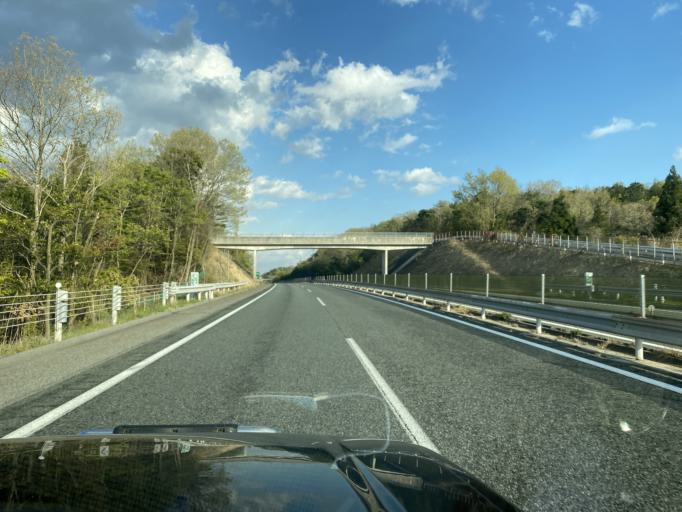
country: JP
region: Hyogo
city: Sandacho
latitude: 34.9458
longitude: 135.1451
